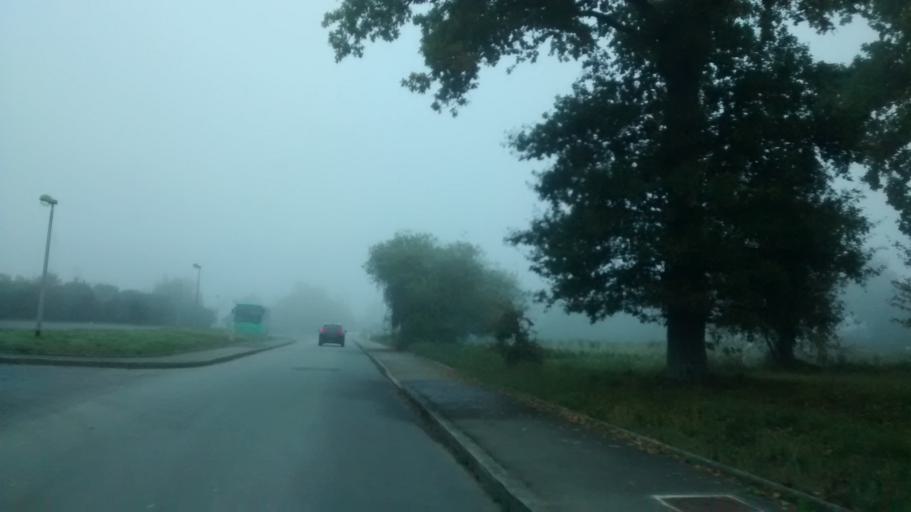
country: FR
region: Brittany
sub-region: Departement d'Ille-et-Vilaine
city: Liffre
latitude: 48.2058
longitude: -1.5041
